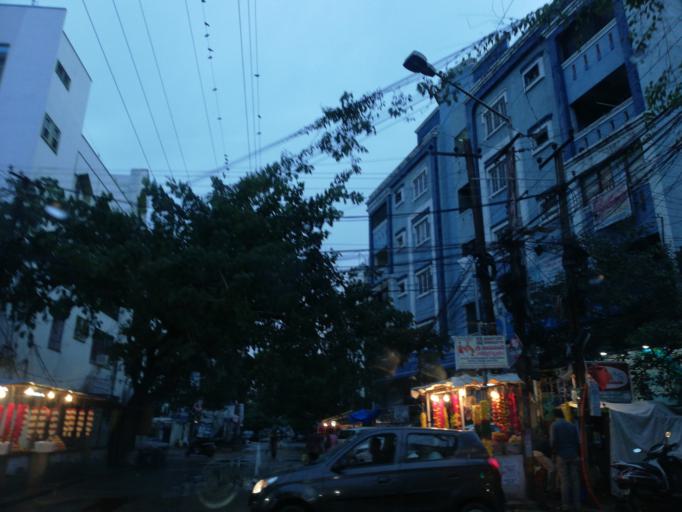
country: IN
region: Telangana
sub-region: Hyderabad
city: Hyderabad
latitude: 17.4247
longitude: 78.4500
